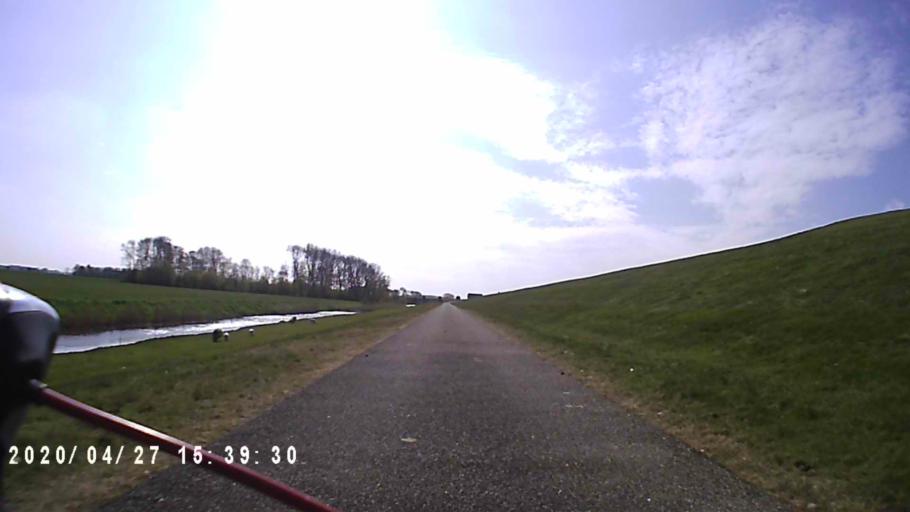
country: NL
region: Groningen
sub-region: Gemeente De Marne
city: Ulrum
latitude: 53.3936
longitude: 6.3134
